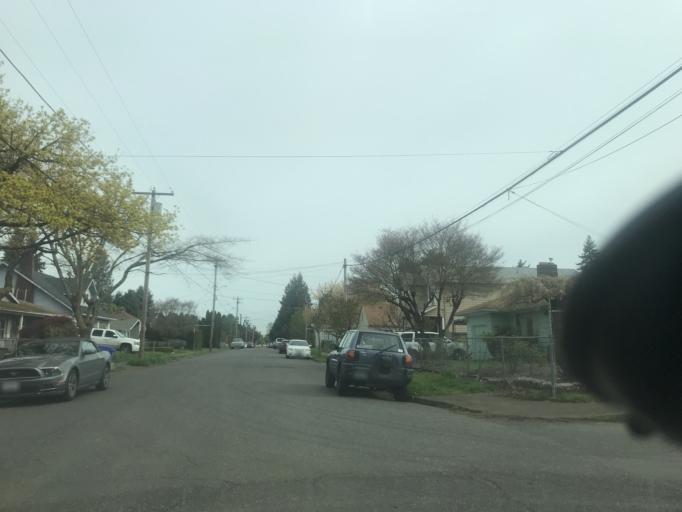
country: US
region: Oregon
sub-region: Multnomah County
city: Lents
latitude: 45.4914
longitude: -122.5810
